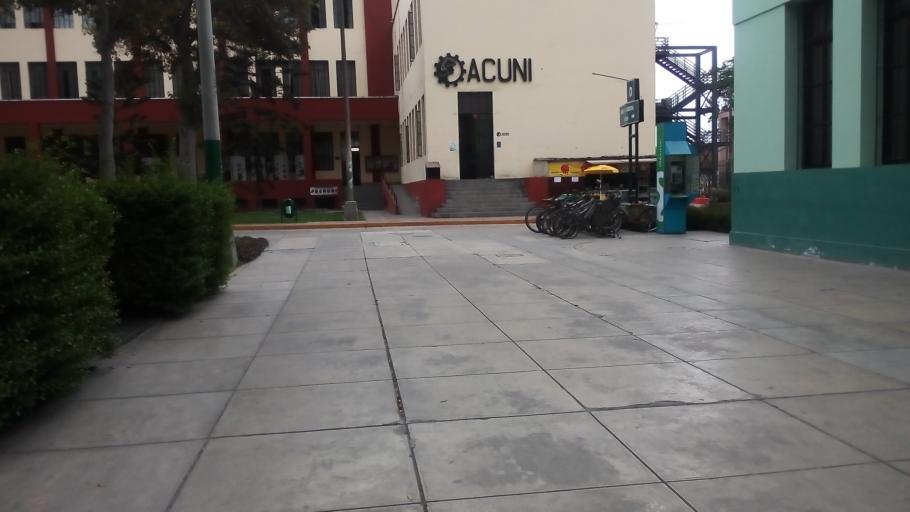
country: PE
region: Lima
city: Lima
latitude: -12.0230
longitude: -77.0483
